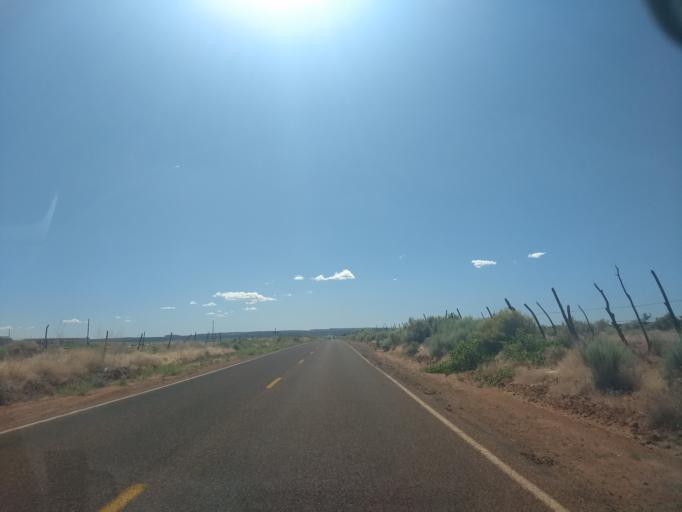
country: US
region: Arizona
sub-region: Mohave County
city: Colorado City
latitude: 36.9469
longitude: -112.9348
